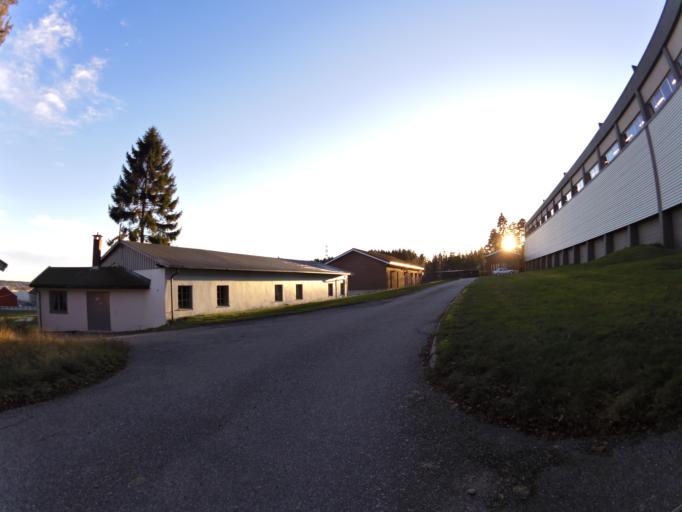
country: NO
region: Ostfold
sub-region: Fredrikstad
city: Fredrikstad
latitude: 59.2457
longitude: 10.9664
